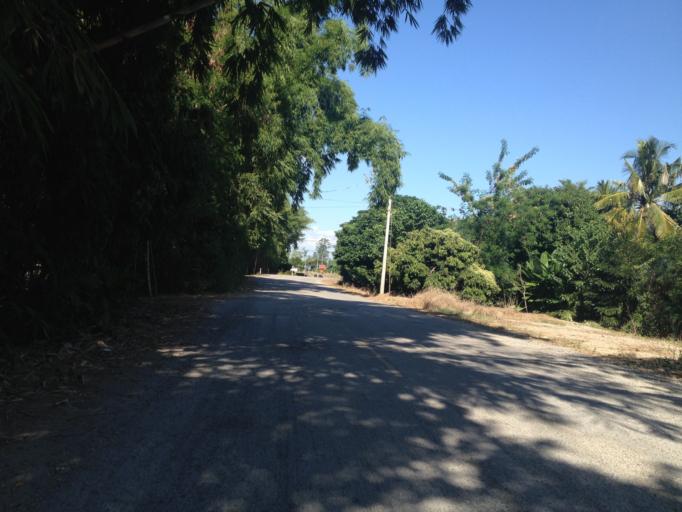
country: TH
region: Chiang Mai
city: Saraphi
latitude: 18.6844
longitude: 98.9873
